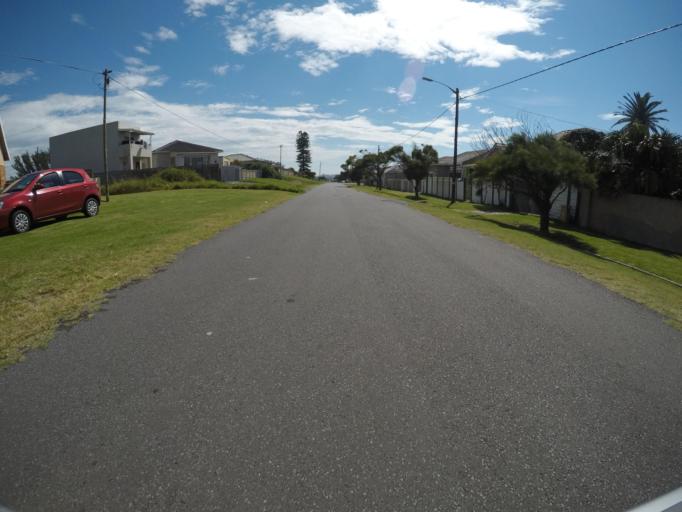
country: ZA
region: Eastern Cape
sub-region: Buffalo City Metropolitan Municipality
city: East London
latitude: -33.0361
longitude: 27.9035
